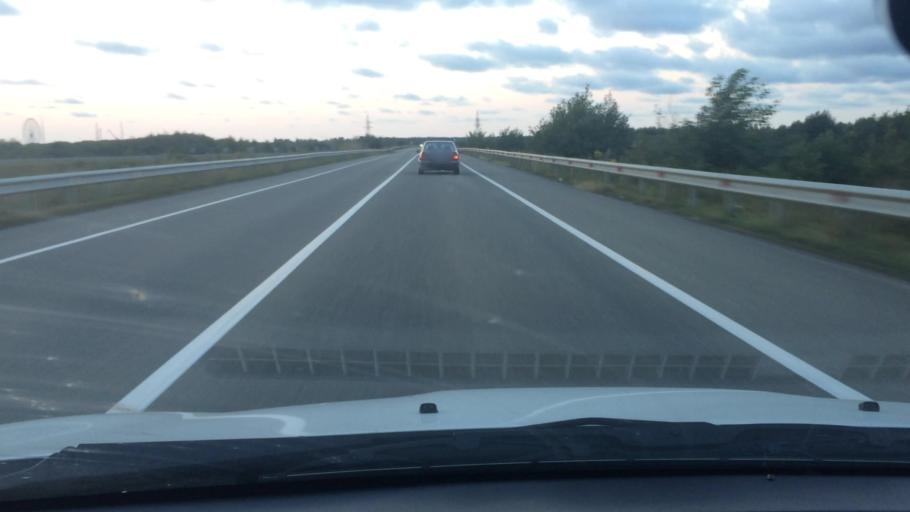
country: GE
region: Ajaria
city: Ochkhamuri
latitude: 41.9012
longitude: 41.7940
